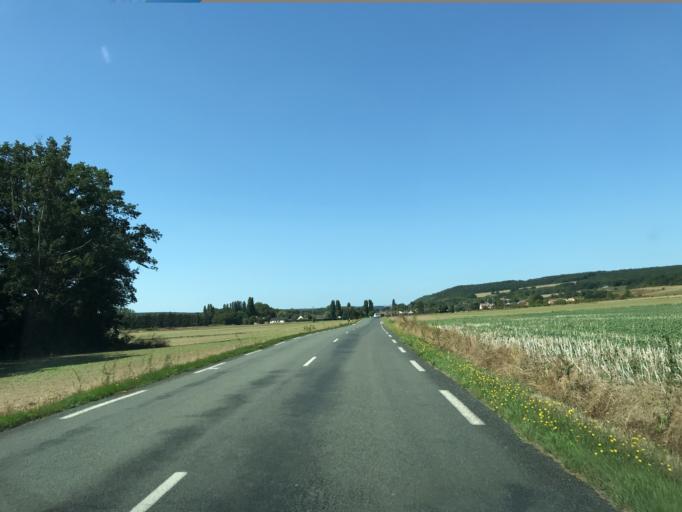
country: FR
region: Haute-Normandie
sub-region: Departement de l'Eure
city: Heudreville-sur-Eure
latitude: 49.1191
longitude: 1.2229
